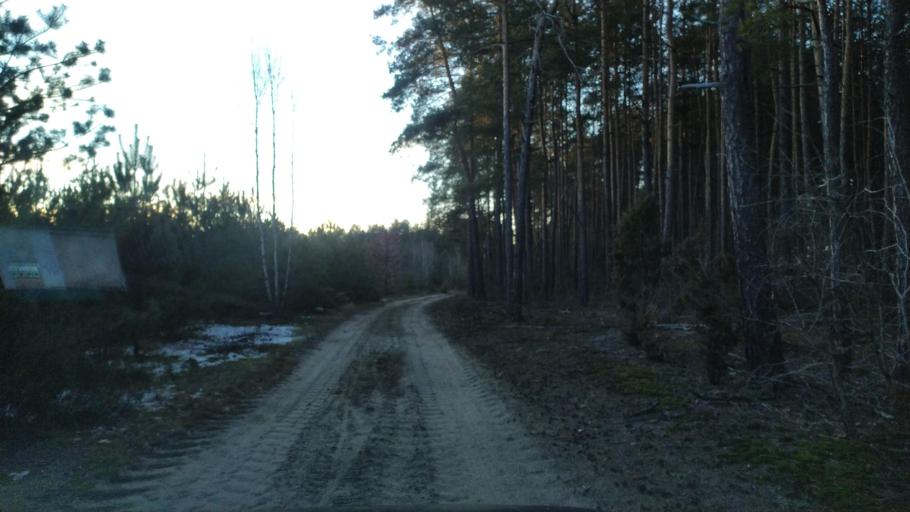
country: BY
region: Brest
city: Pruzhany
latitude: 52.5517
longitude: 24.2742
